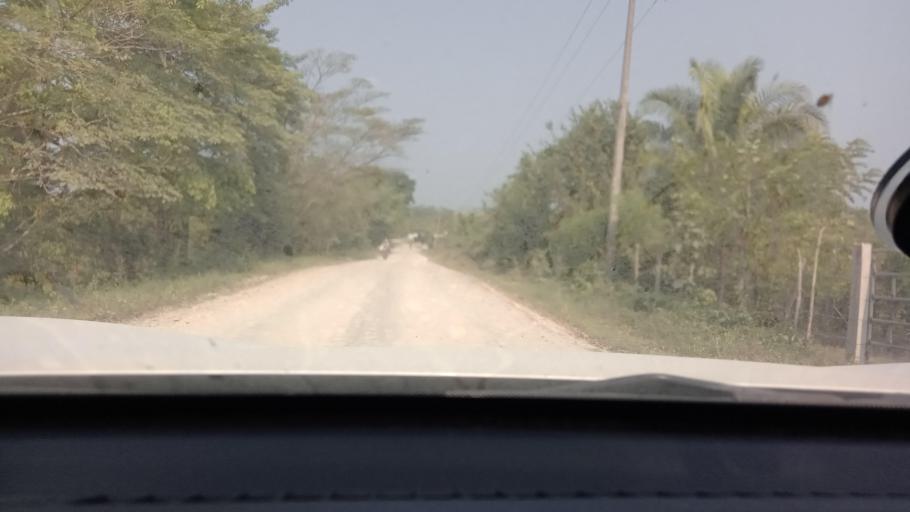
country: MX
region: Tabasco
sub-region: Huimanguillo
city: Francisco Rueda
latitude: 17.6119
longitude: -93.9350
